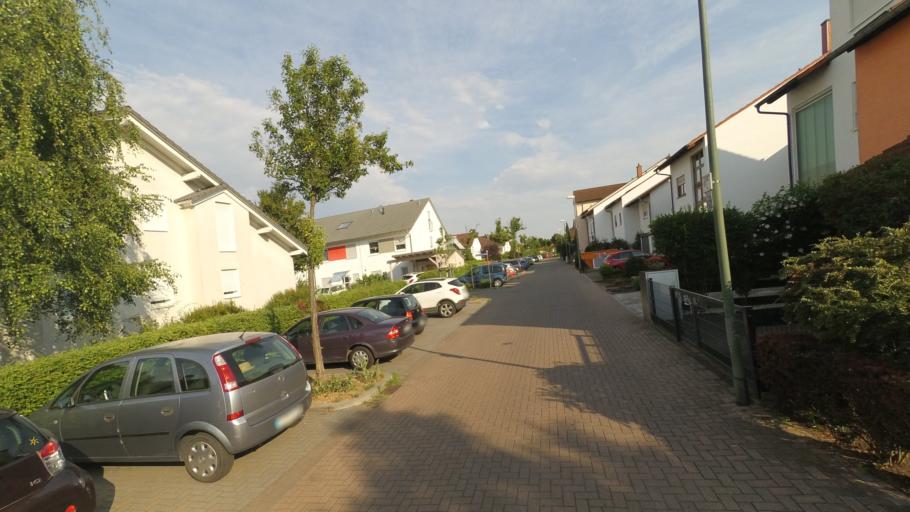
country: DE
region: Rheinland-Pfalz
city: Gartenstadt
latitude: 49.4541
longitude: 8.3985
